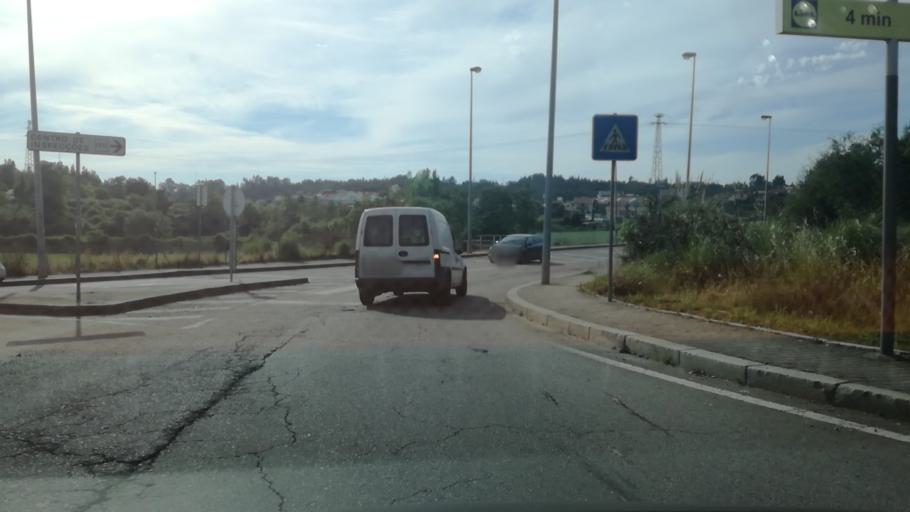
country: PT
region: Porto
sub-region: Valongo
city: Ermesinde
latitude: 41.2215
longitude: -8.5630
